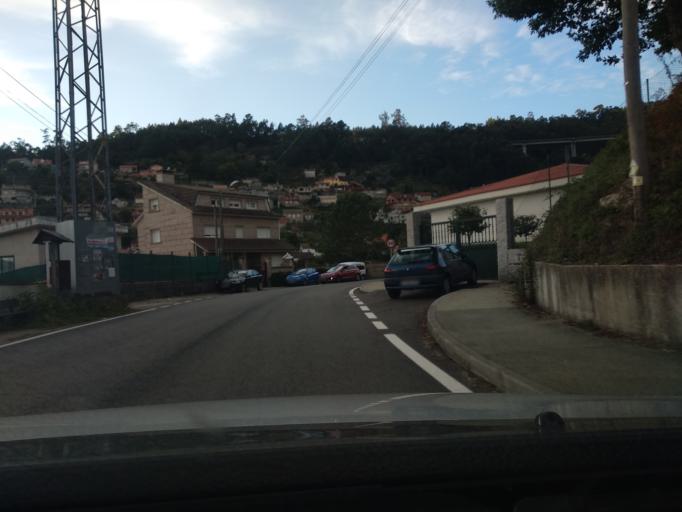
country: ES
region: Galicia
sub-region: Provincia de Pontevedra
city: Redondela
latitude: 42.2937
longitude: -8.6795
